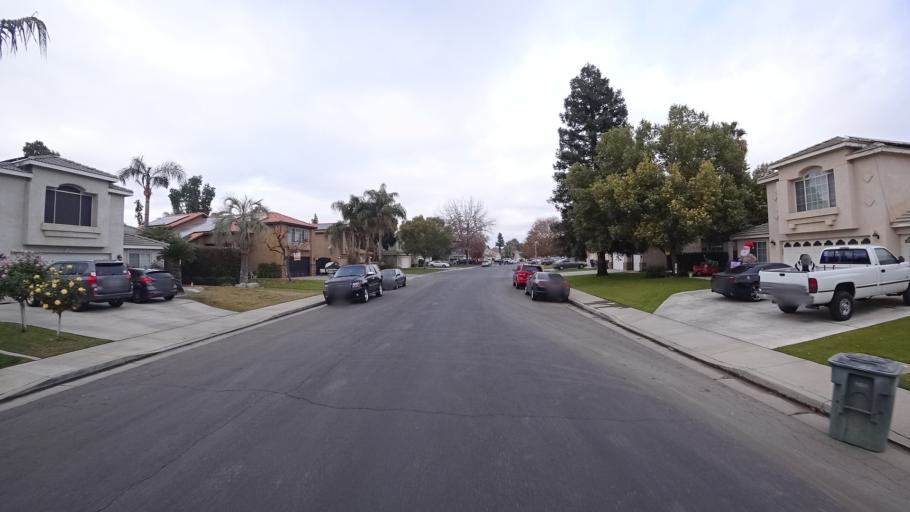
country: US
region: California
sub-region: Kern County
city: Greenacres
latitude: 35.3002
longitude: -119.0870
